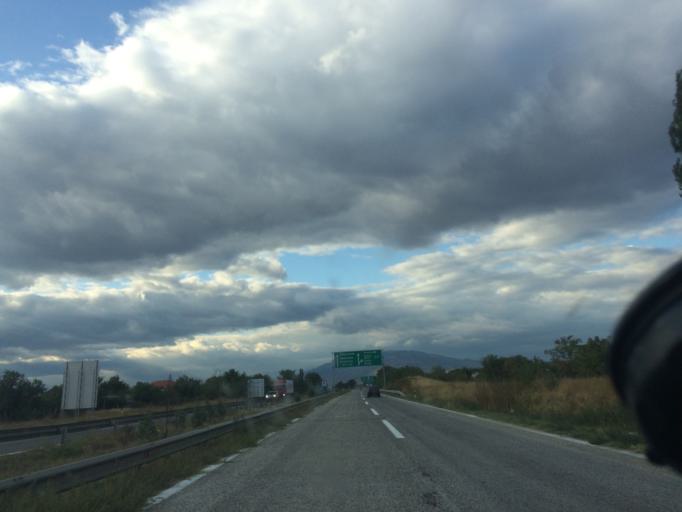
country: MK
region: Petrovec
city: Petrovec
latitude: 41.9272
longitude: 21.6316
